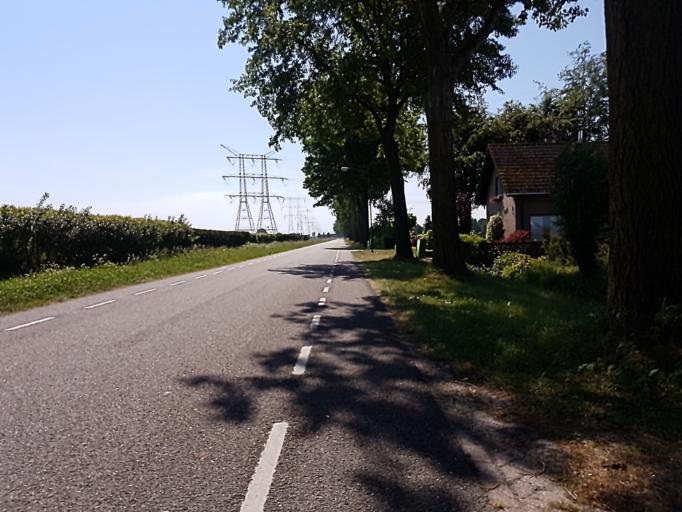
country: NL
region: North Brabant
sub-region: Gemeente Dongen
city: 's Gravenmoer
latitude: 51.6539
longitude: 4.9876
